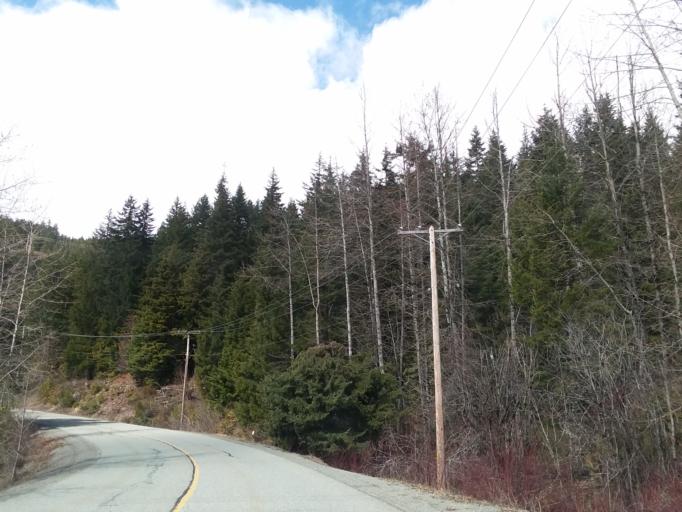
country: CA
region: British Columbia
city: Whistler
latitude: 50.1035
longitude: -122.9961
